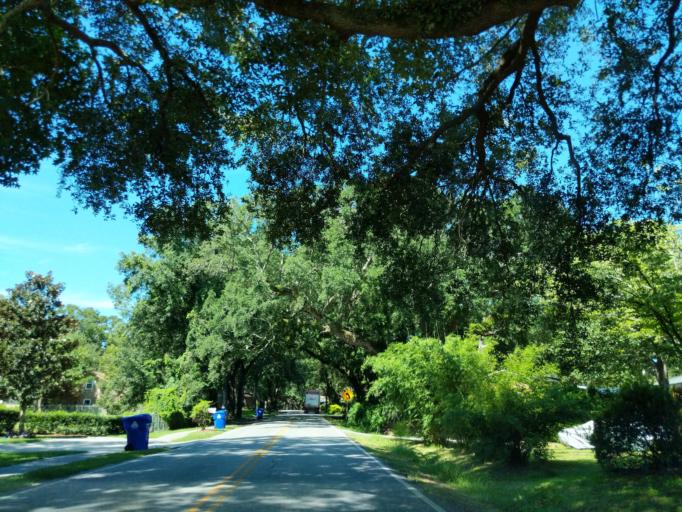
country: US
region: South Carolina
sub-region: Charleston County
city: Charleston
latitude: 32.7395
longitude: -79.9191
